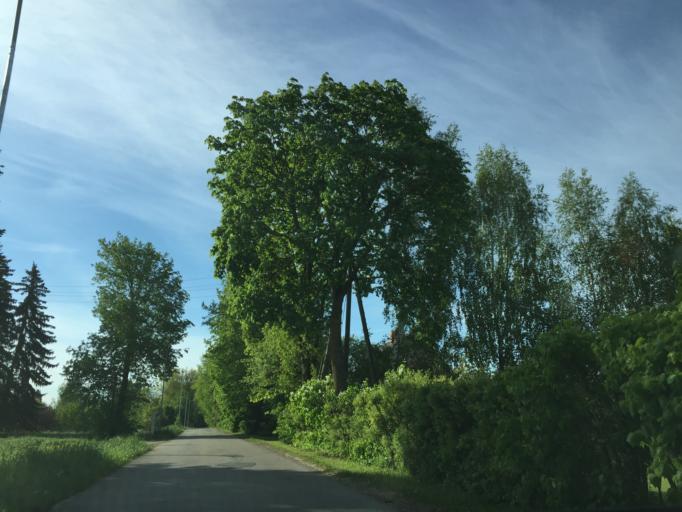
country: LV
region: Bauskas Rajons
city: Bauska
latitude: 56.4688
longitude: 24.1735
